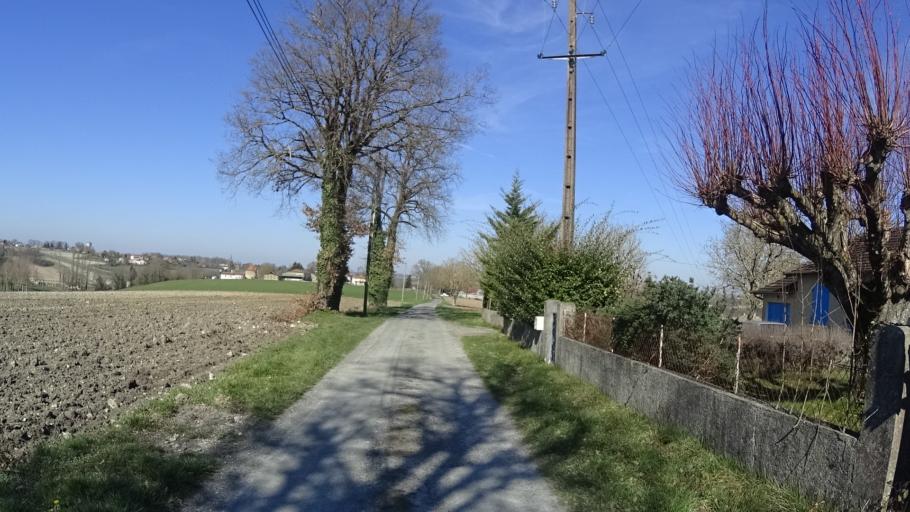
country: FR
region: Aquitaine
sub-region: Departement de la Dordogne
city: Riberac
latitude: 45.2337
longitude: 0.3412
